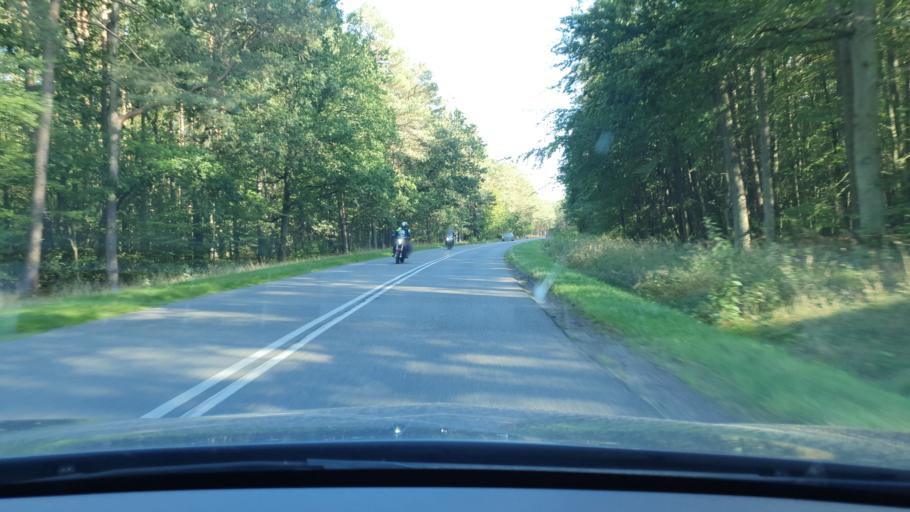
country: PL
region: West Pomeranian Voivodeship
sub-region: Powiat goleniowski
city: Przybiernow
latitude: 53.8248
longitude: 14.8049
